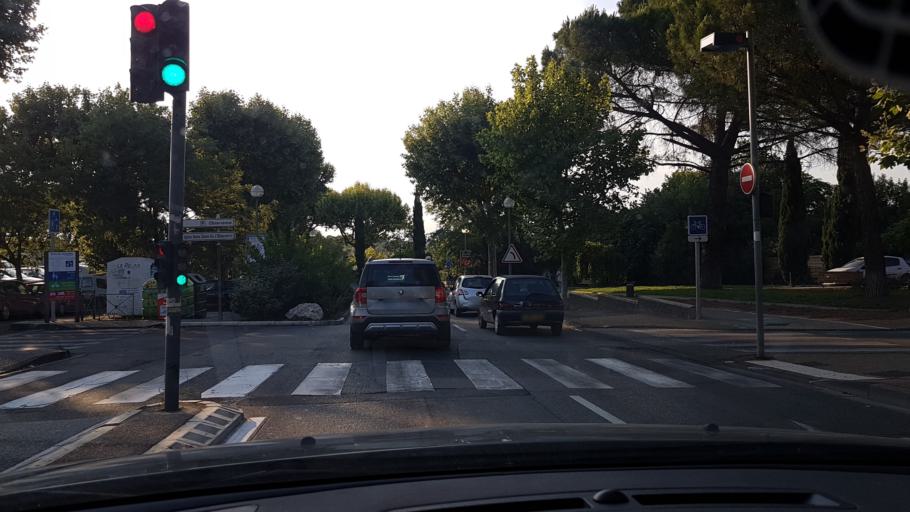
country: FR
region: Provence-Alpes-Cote d'Azur
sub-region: Departement du Vaucluse
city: Carpentras
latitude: 44.0577
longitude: 5.0506
